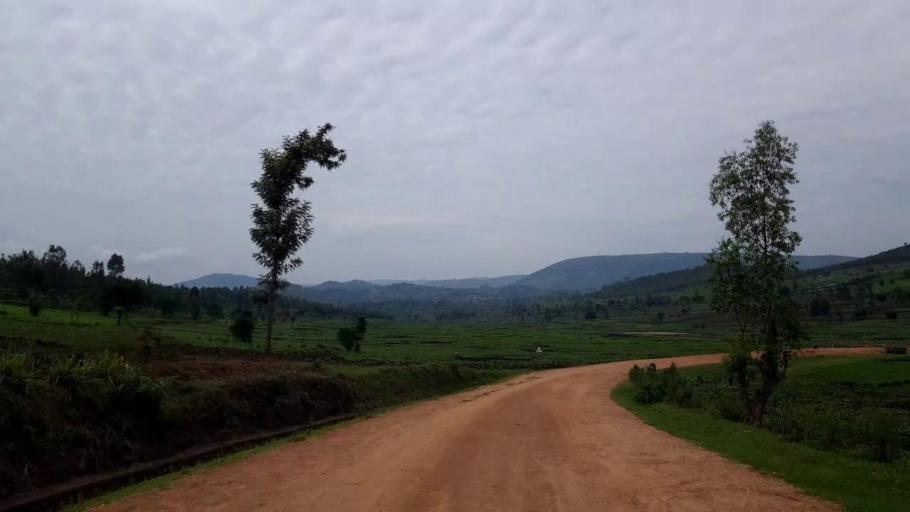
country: RW
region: Northern Province
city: Byumba
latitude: -1.5002
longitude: 30.2314
